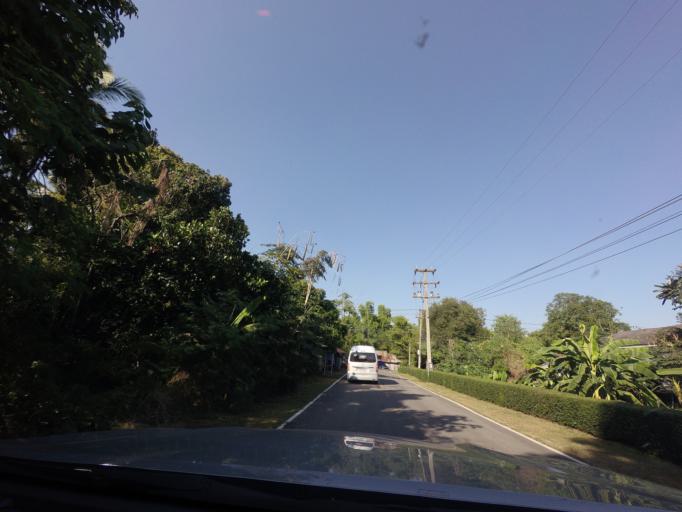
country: TH
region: Sukhothai
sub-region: Amphoe Si Satchanalai
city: Si Satchanalai
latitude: 17.4310
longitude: 99.7918
